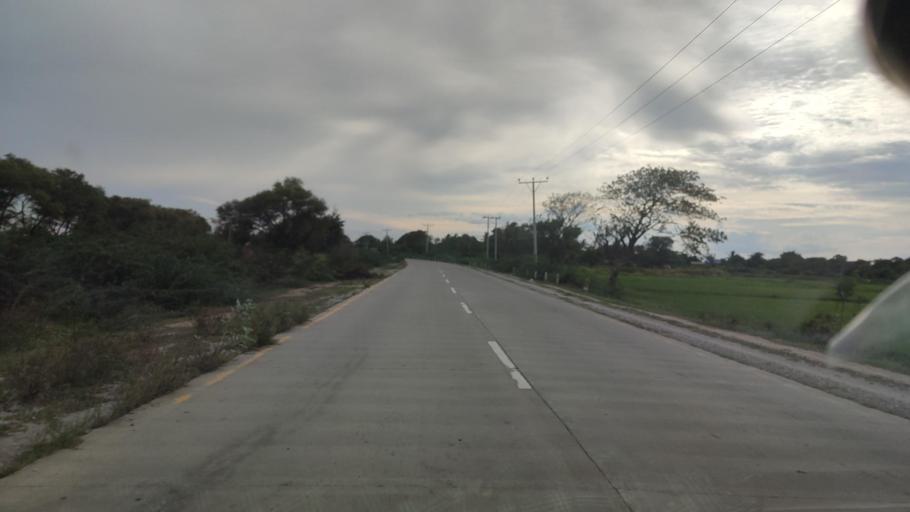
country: MM
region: Mandalay
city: Kyaukse
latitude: 21.3268
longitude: 96.0302
